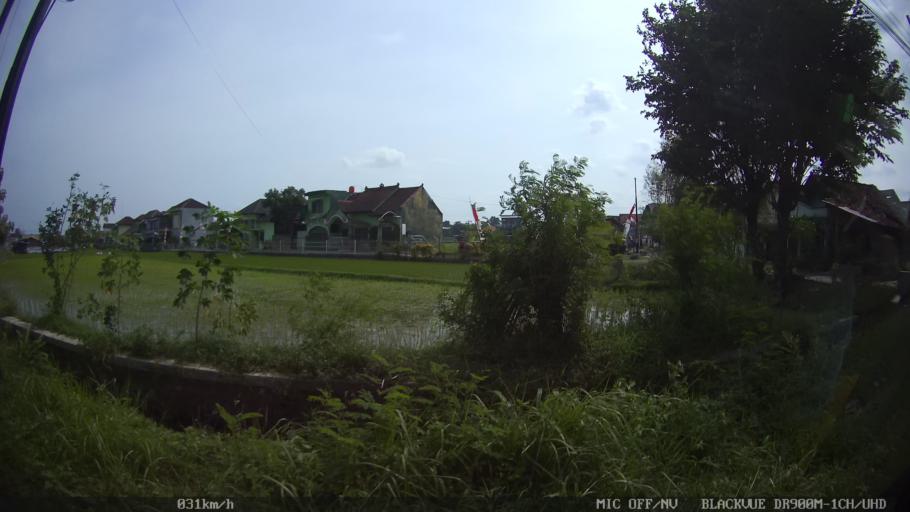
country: ID
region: Daerah Istimewa Yogyakarta
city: Depok
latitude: -7.8034
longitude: 110.4457
